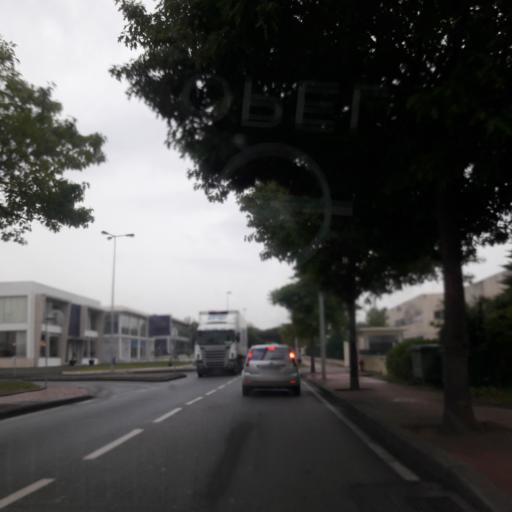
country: PT
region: Porto
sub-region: Vila do Conde
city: Arvore
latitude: 41.3314
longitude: -8.7198
